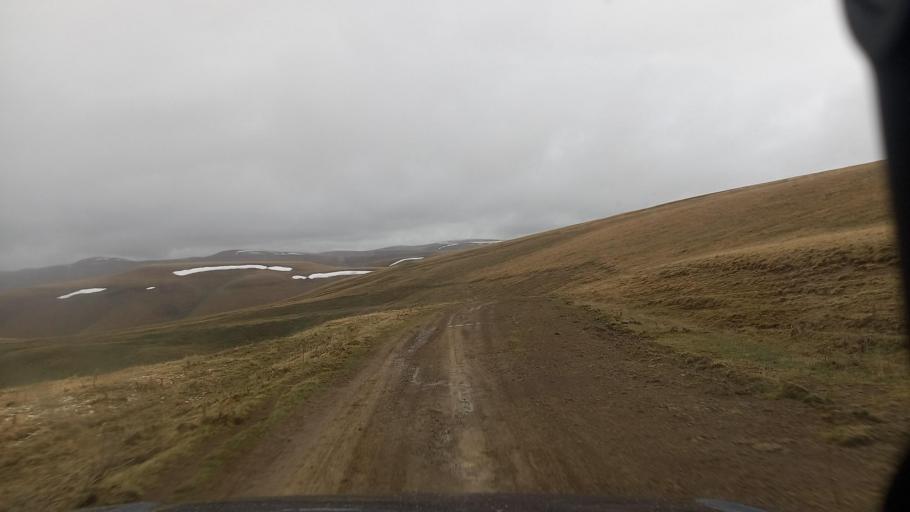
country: RU
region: Kabardino-Balkariya
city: Terskol
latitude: 43.5872
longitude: 42.4654
